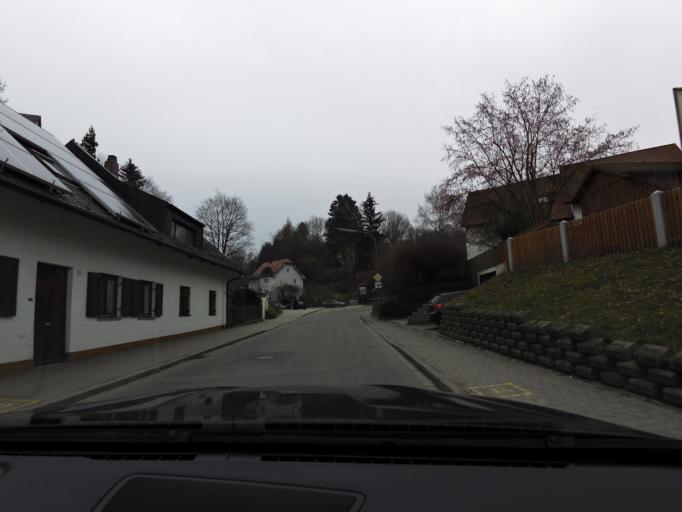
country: DE
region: Bavaria
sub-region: Lower Bavaria
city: Landshut
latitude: 48.5344
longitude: 12.1706
